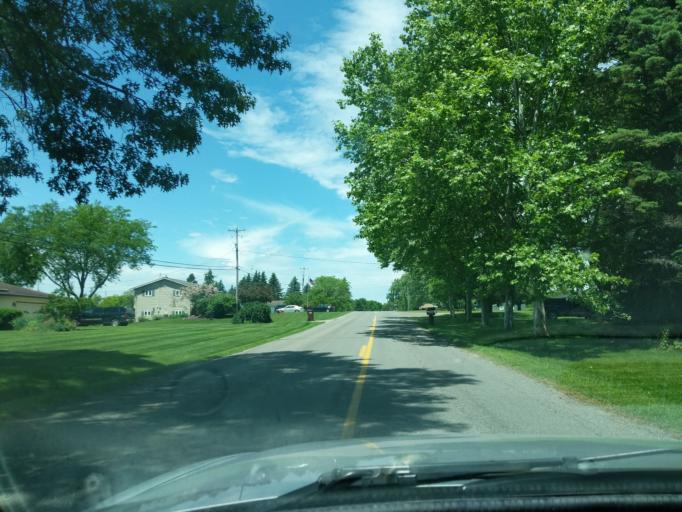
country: US
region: Michigan
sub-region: Jackson County
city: Michigan Center
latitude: 42.1919
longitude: -84.3070
